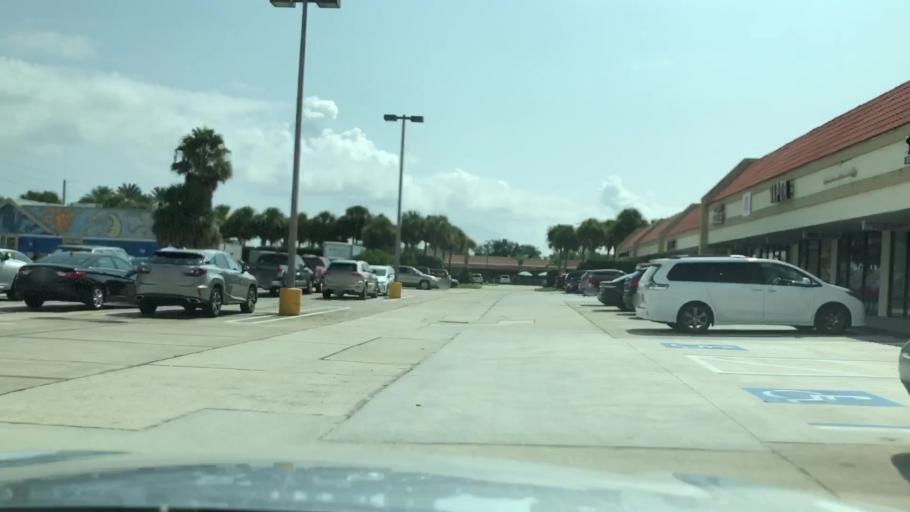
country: US
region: Florida
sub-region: Duval County
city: Atlantic Beach
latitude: 30.3237
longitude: -81.4154
